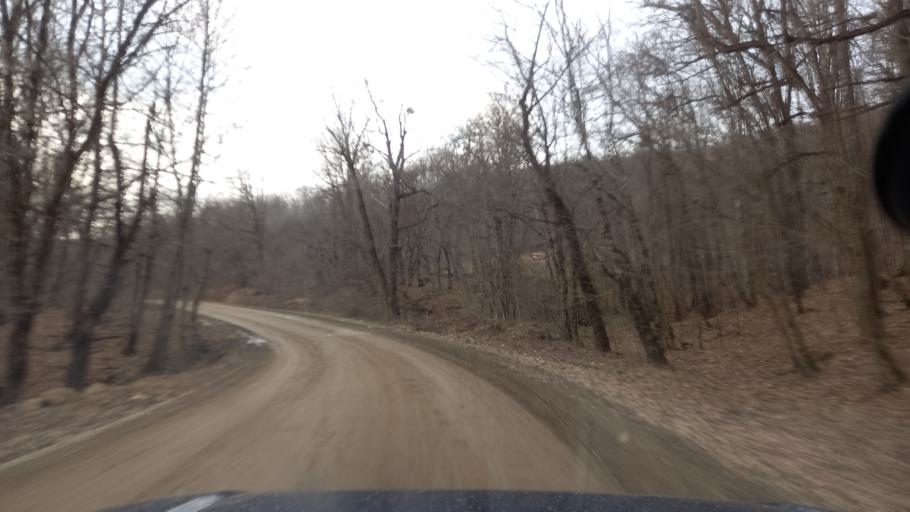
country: RU
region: Adygeya
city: Kamennomostskiy
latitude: 44.1420
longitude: 40.2736
